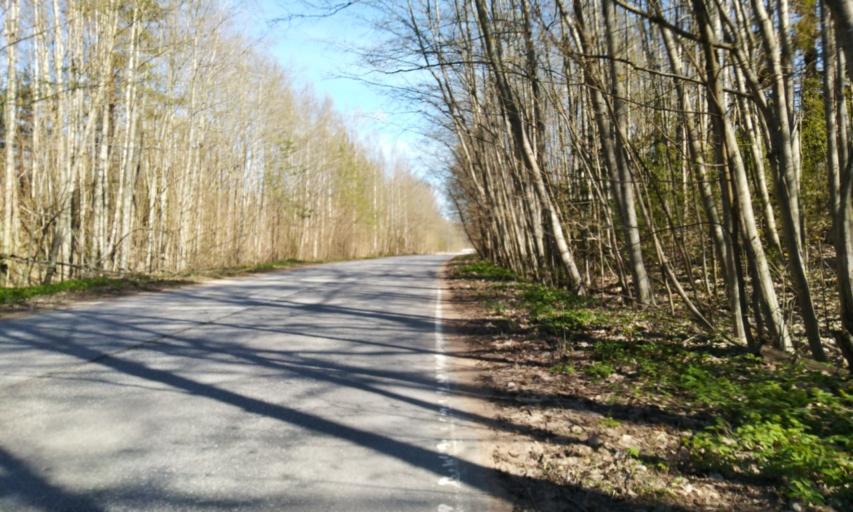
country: RU
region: Leningrad
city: Garbolovo
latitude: 60.4121
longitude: 30.4581
